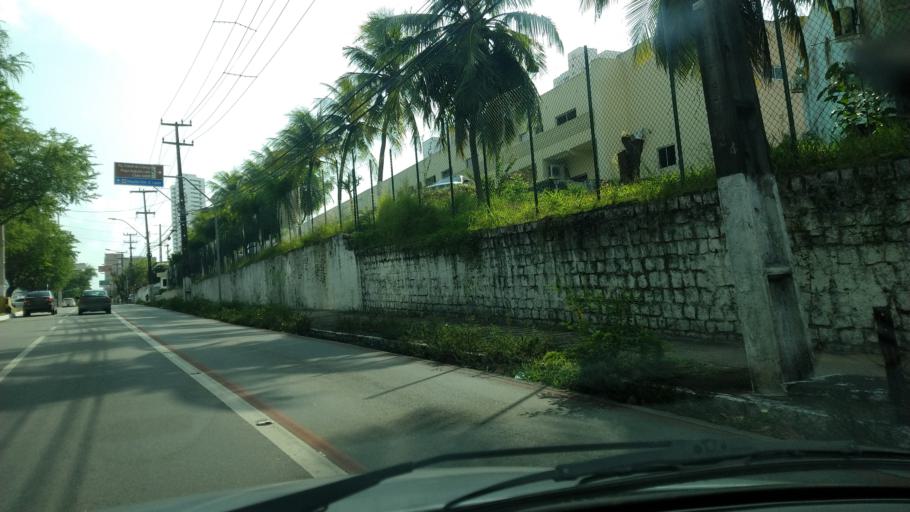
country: BR
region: Rio Grande do Norte
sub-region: Natal
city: Natal
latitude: -5.7954
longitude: -35.2041
